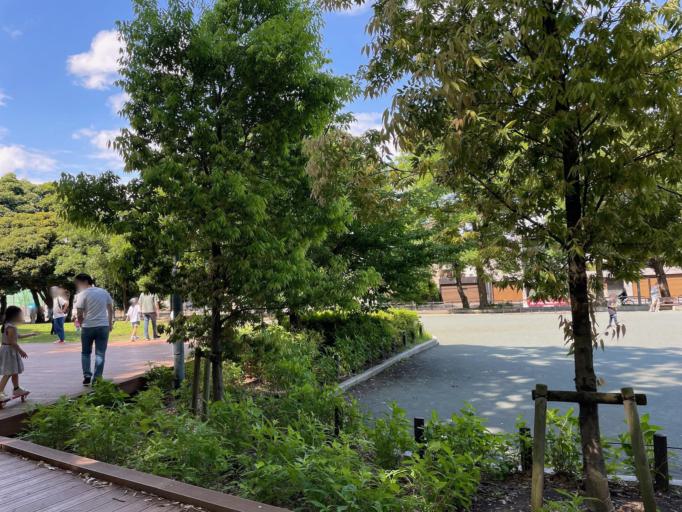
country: JP
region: Tokyo
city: Mitaka-shi
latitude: 35.6654
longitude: 139.6218
